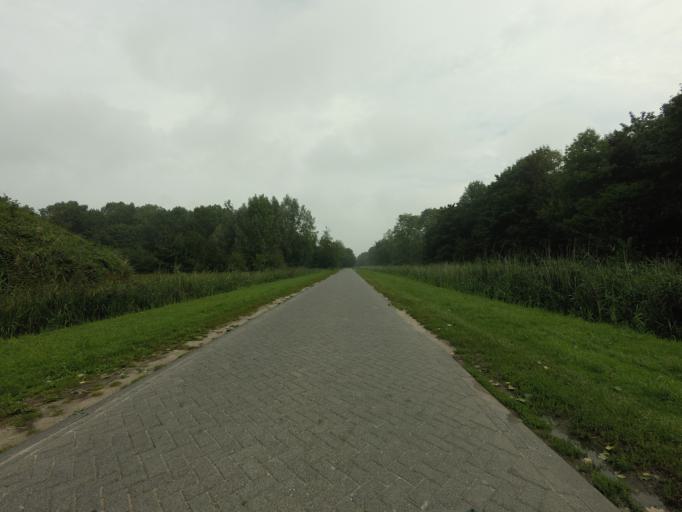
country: NL
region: North Holland
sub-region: Gemeente Huizen
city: Huizen
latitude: 52.3232
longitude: 5.2921
